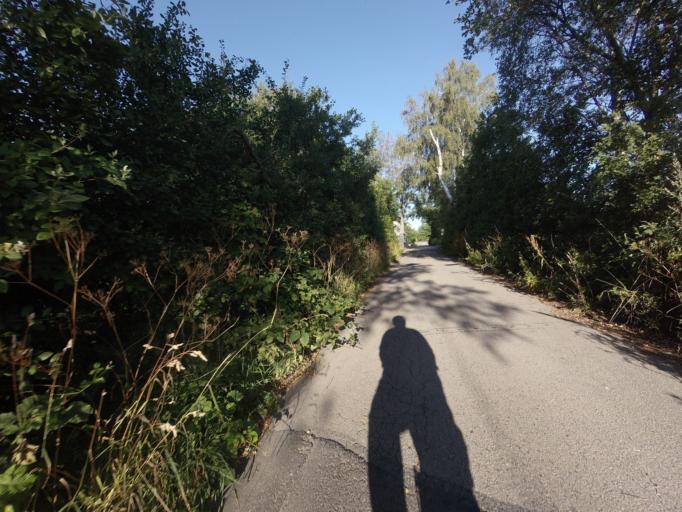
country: SE
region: Skane
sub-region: Hoganas Kommun
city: Hoganas
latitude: 56.1430
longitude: 12.5872
